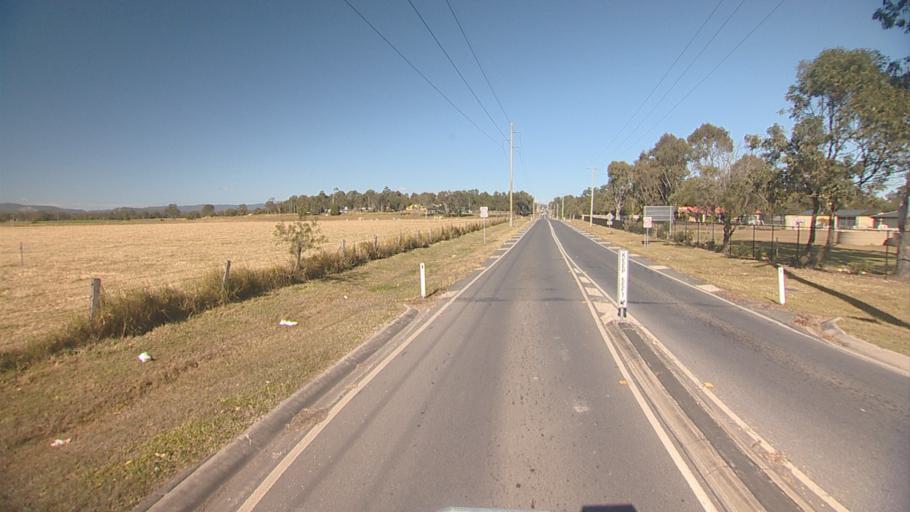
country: AU
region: Queensland
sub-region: Logan
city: Chambers Flat
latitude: -27.7533
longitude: 153.0922
